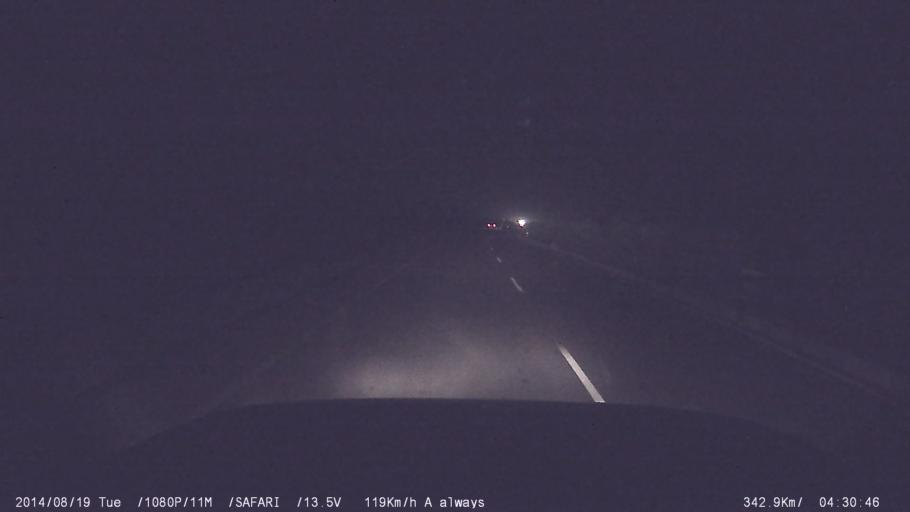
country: IN
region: Tamil Nadu
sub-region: Erode
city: Perundurai
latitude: 11.2697
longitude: 77.5539
